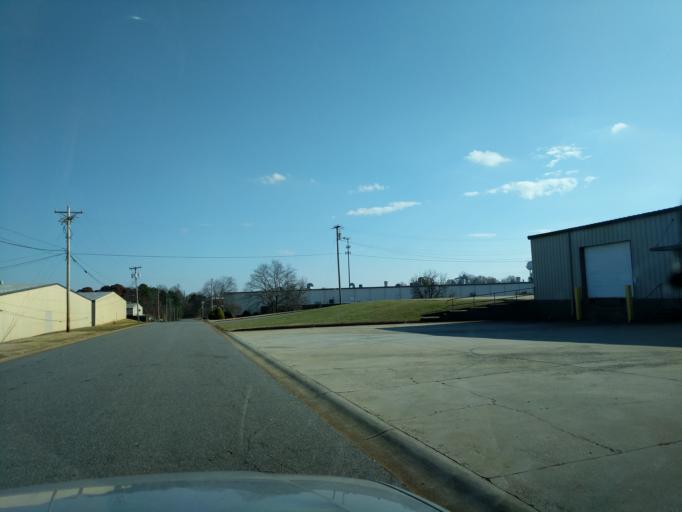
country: US
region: North Carolina
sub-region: Iredell County
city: Statesville
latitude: 35.7917
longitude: -80.9226
